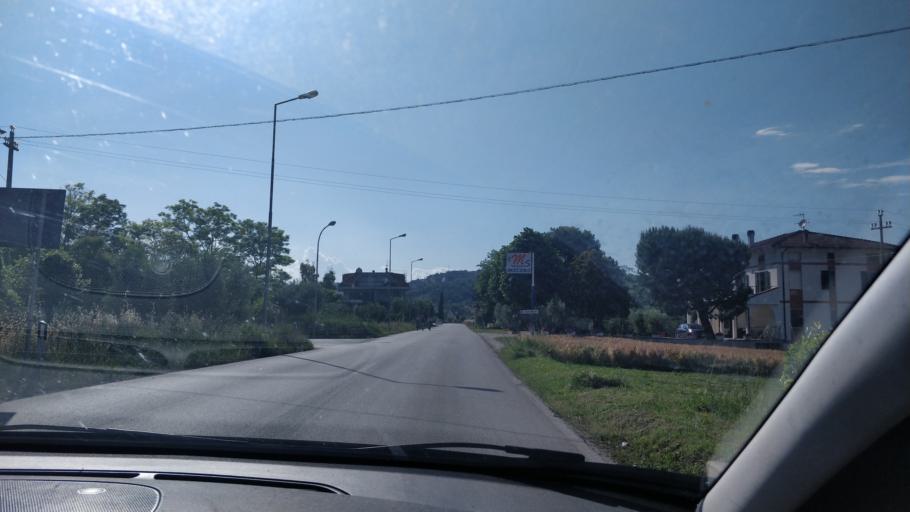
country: IT
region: The Marches
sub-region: Provincia di Ascoli Piceno
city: Cupra Marittima
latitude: 43.0357
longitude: 13.8368
